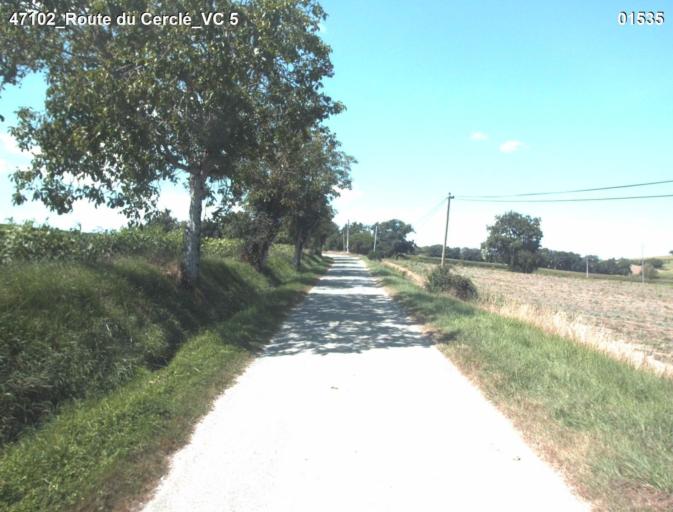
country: FR
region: Aquitaine
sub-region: Departement du Lot-et-Garonne
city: Laplume
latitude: 44.0749
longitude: 0.4448
